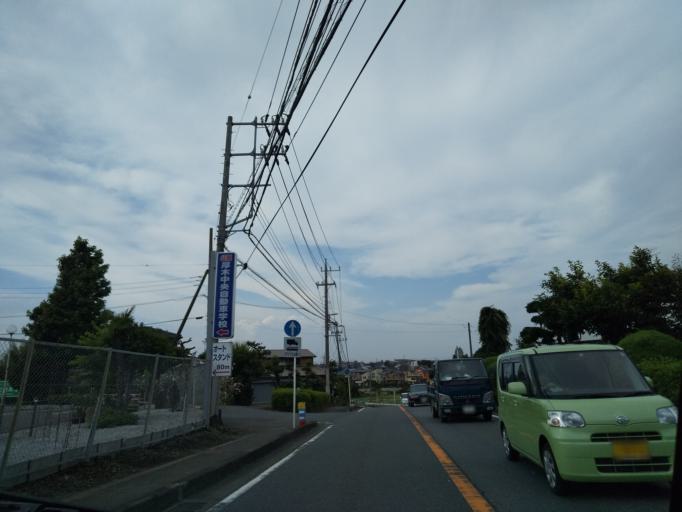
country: JP
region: Kanagawa
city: Atsugi
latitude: 35.4711
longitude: 139.3406
